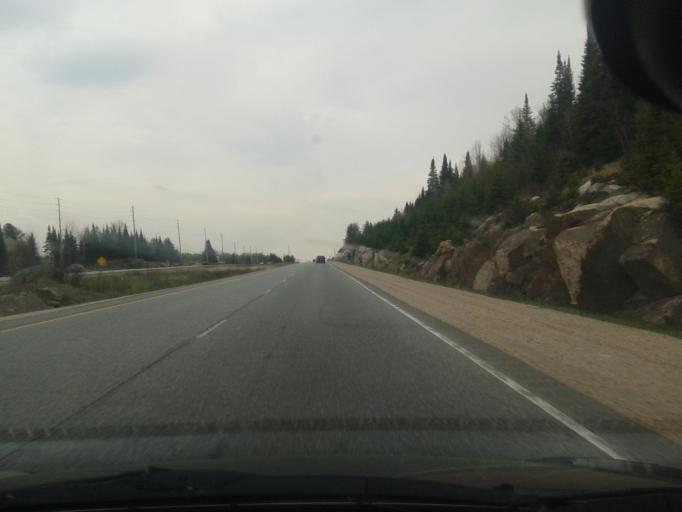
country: CA
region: Ontario
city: Powassan
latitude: 46.1792
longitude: -79.3594
